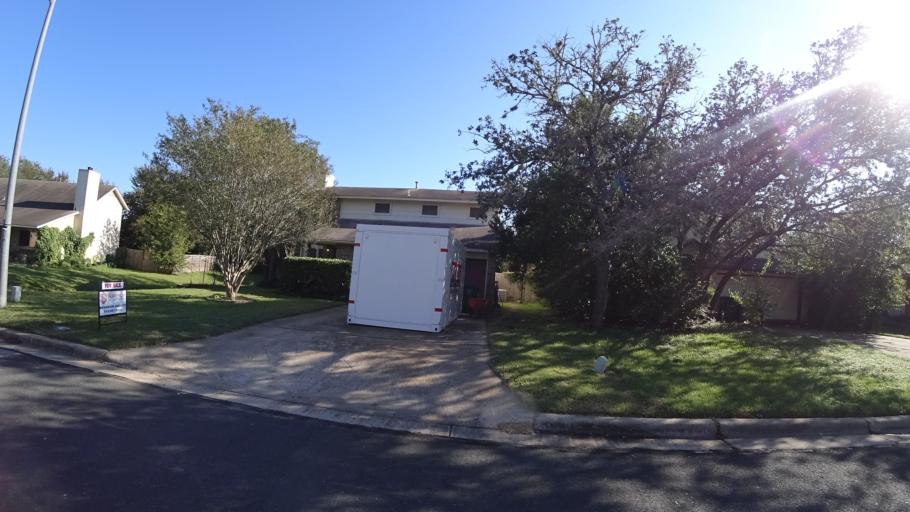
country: US
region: Texas
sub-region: Travis County
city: Shady Hollow
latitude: 30.2085
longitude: -97.8477
